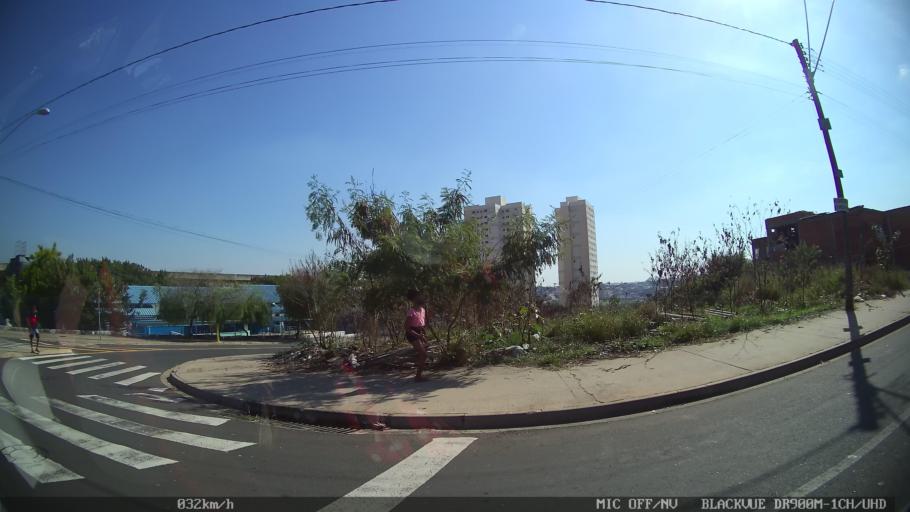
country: BR
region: Sao Paulo
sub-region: Campinas
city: Campinas
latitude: -22.9531
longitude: -47.0784
